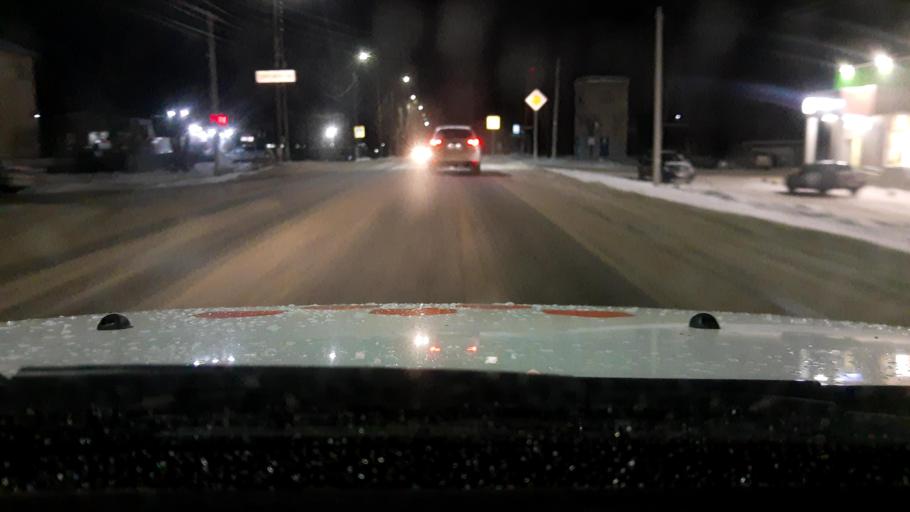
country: RU
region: Nizjnij Novgorod
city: Gorodets
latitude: 56.6565
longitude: 43.4862
